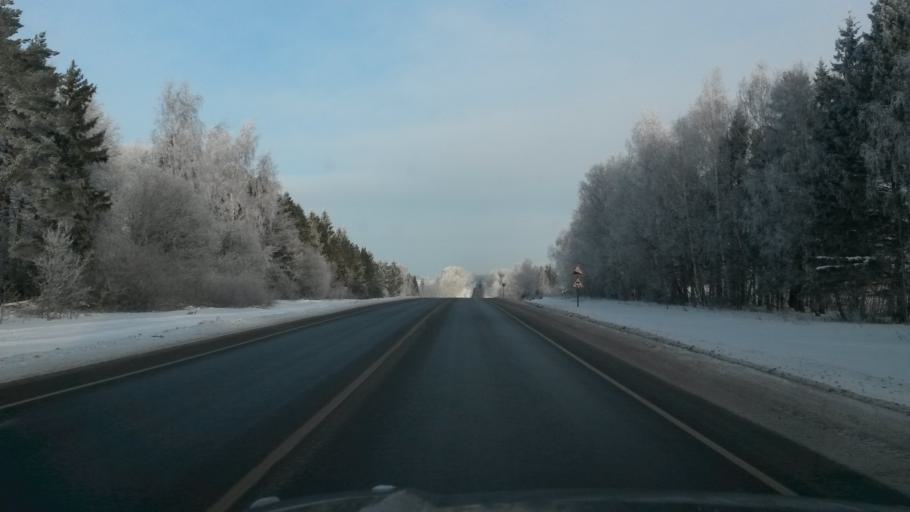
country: RU
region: Vladimir
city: Bogolyubovo
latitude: 56.2380
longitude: 40.4511
